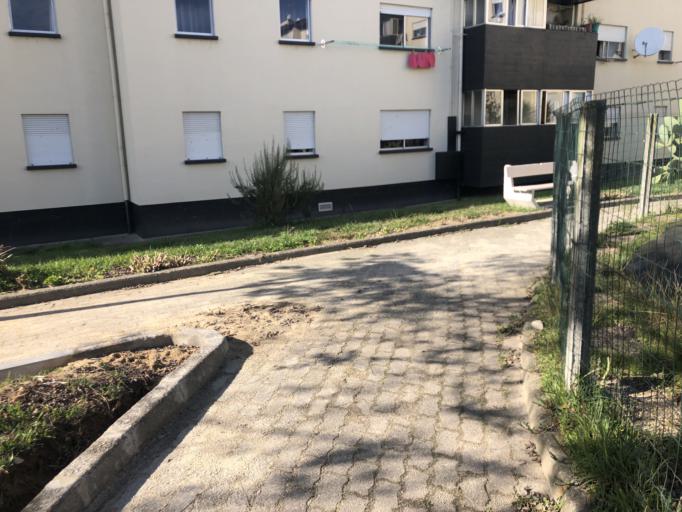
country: PT
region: Aveiro
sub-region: Estarreja
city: Estarreja
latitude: 40.7598
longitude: -8.5749
